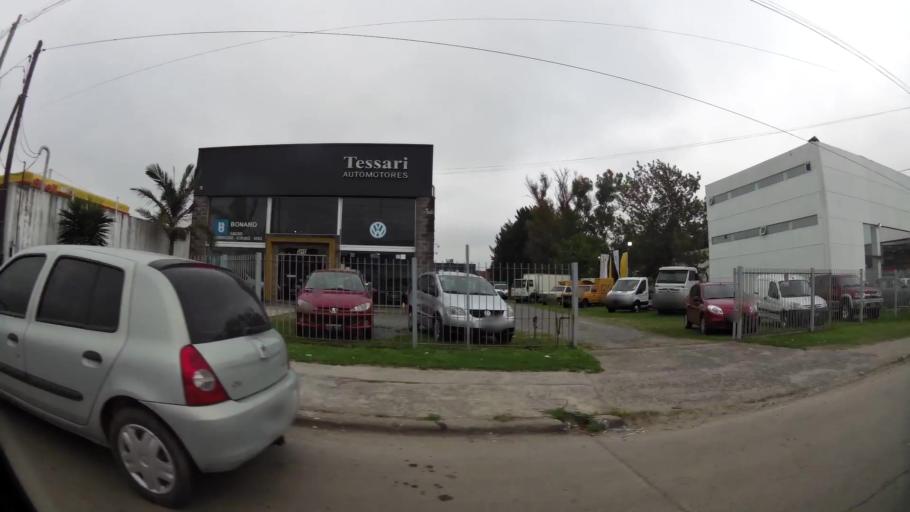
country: AR
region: Buenos Aires
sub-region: Partido de La Plata
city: La Plata
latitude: -34.9434
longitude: -57.9912
